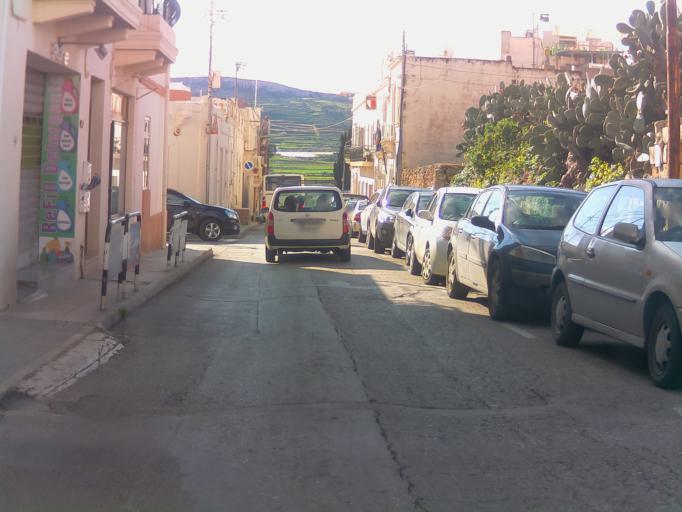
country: MT
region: L-Imgarr
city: Imgarr
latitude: 35.9204
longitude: 14.3671
